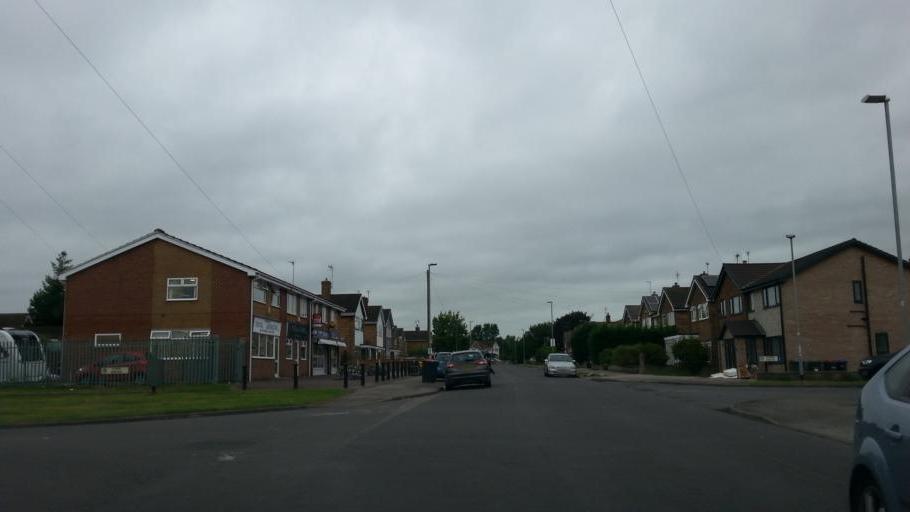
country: GB
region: England
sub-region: Nottinghamshire
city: Hucknall
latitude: 53.0478
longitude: -1.1942
